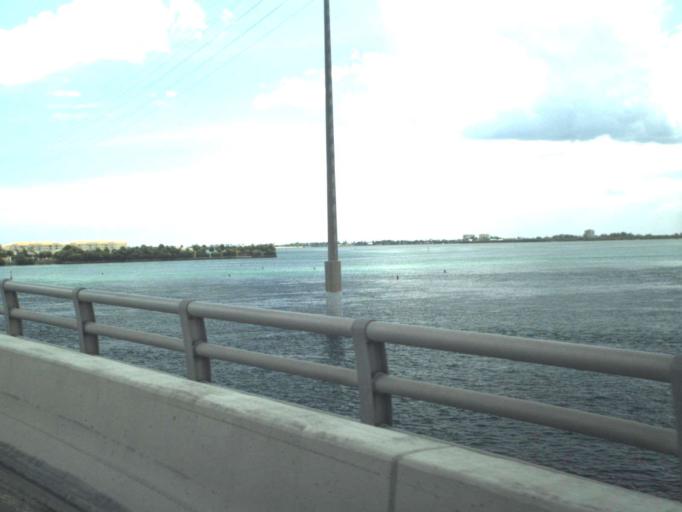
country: US
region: Florida
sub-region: Saint Lucie County
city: Fort Pierce
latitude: 27.4562
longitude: -80.3224
